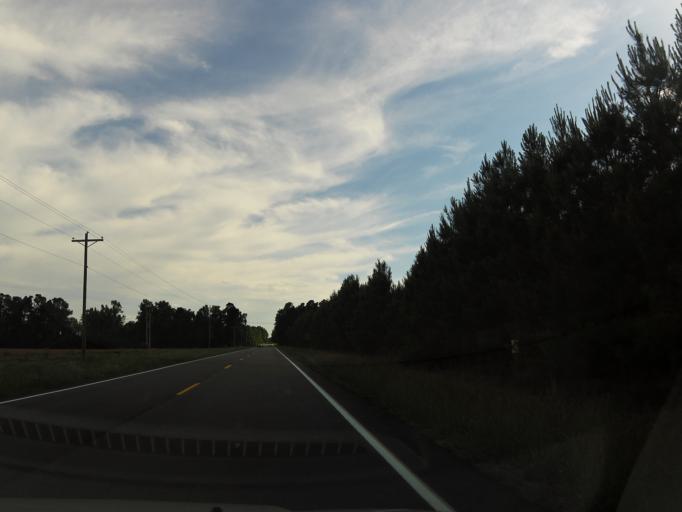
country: US
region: South Carolina
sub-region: Allendale County
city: Fairfax
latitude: 32.9819
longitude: -81.2271
